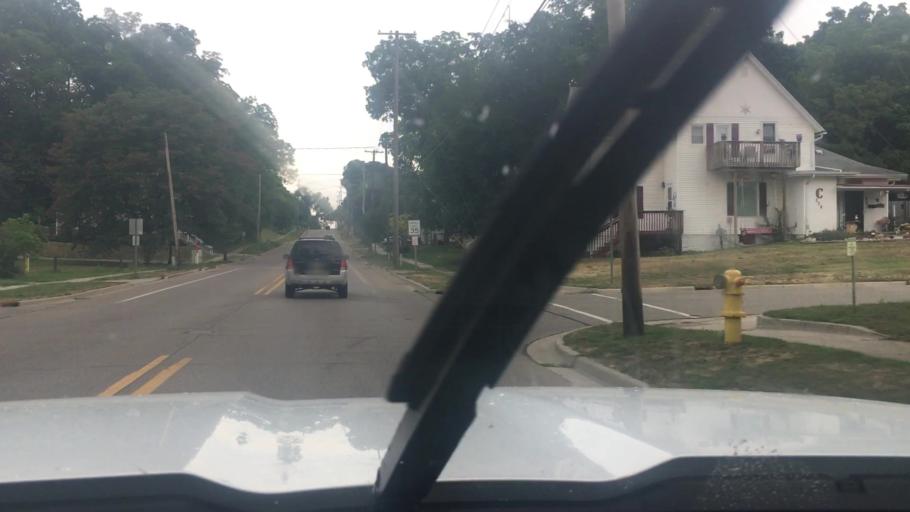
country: US
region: Michigan
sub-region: Ionia County
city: Ionia
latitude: 42.9874
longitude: -85.0584
